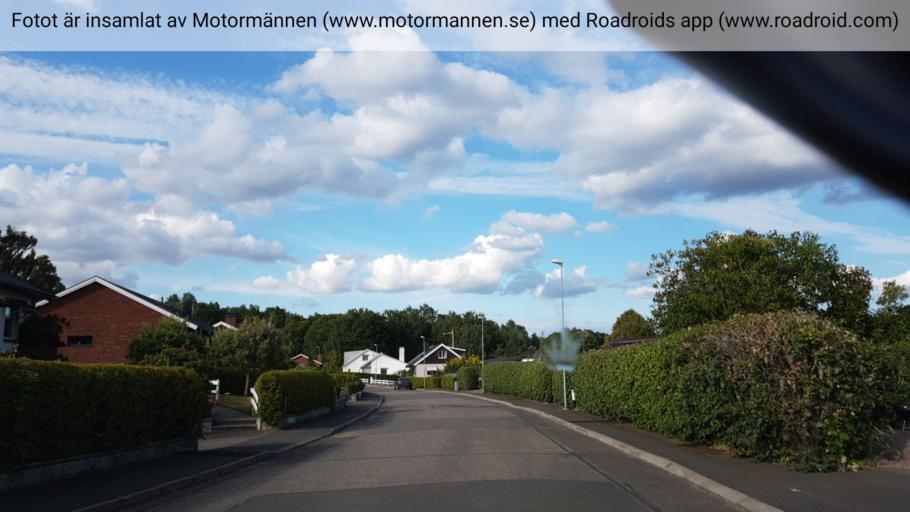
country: SE
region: Vaestra Goetaland
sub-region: Skovde Kommun
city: Skoevde
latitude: 58.3955
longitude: 13.8237
